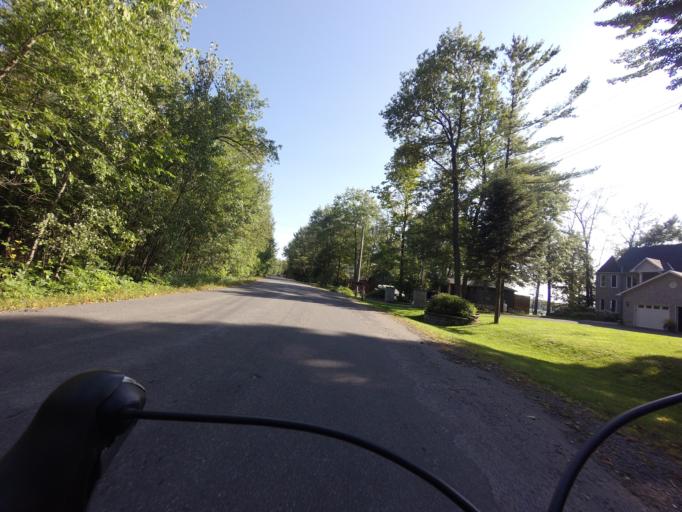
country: CA
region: Ontario
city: Bells Corners
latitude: 45.4832
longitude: -76.0517
